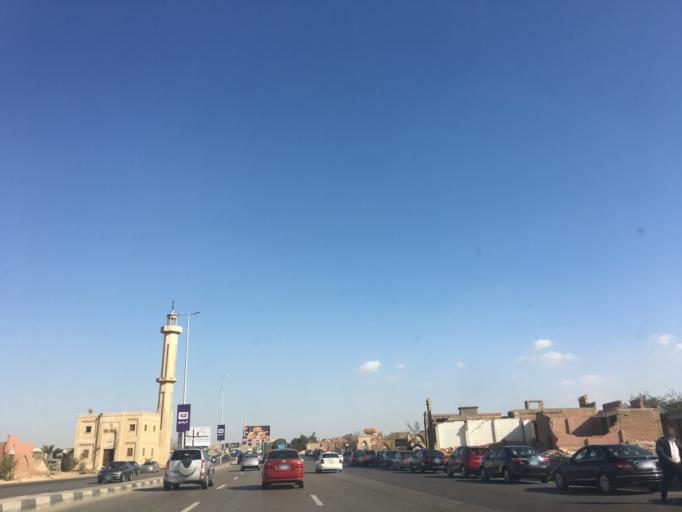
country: EG
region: Muhafazat al Qahirah
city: Cairo
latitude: 30.0221
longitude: 31.3497
